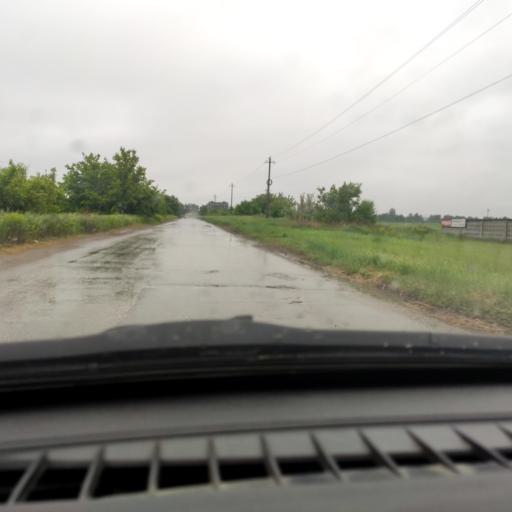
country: RU
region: Samara
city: Tol'yatti
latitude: 53.5678
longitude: 49.3598
